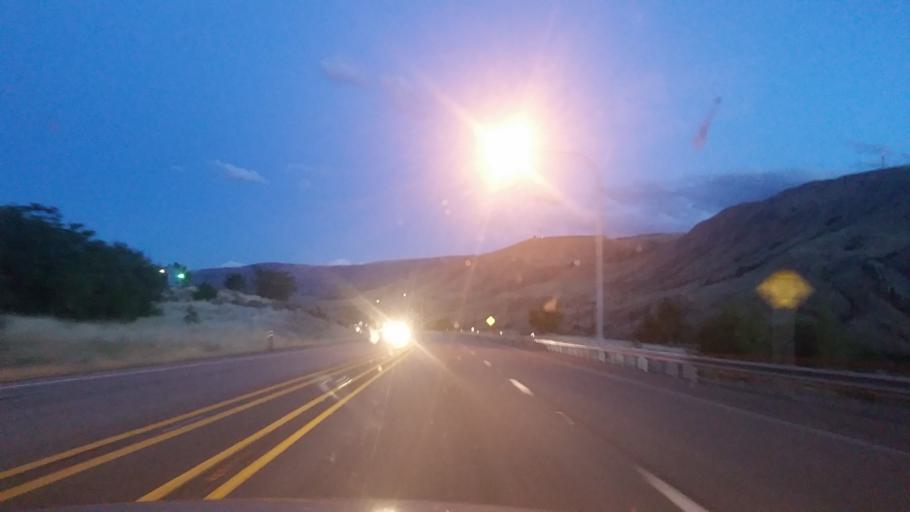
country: US
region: Washington
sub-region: Chelan County
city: South Wenatchee
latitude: 47.3979
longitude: -120.2861
